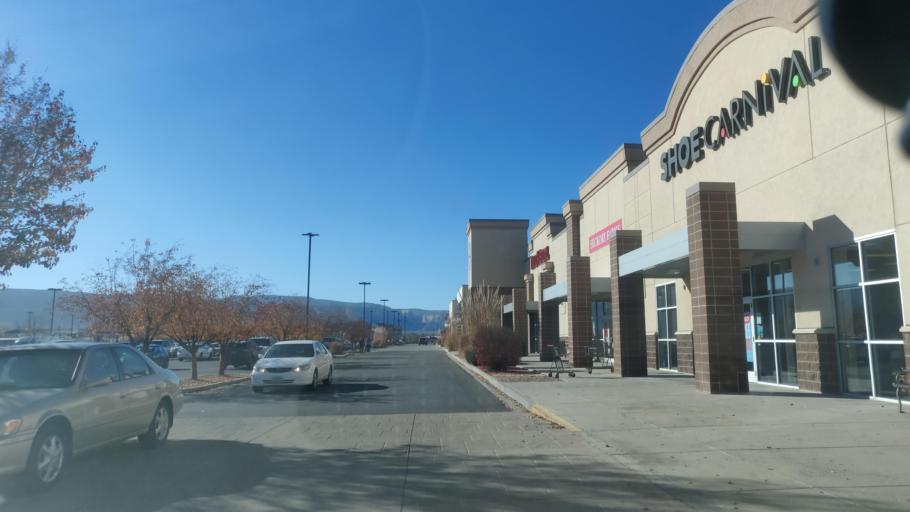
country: US
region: Colorado
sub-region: Mesa County
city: Redlands
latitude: 39.0964
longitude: -108.6041
